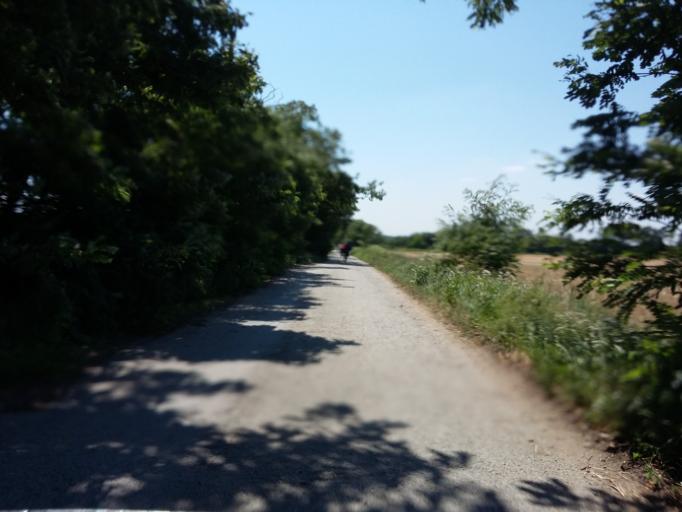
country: AT
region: Lower Austria
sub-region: Politischer Bezirk Ganserndorf
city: Marchegg
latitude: 48.2879
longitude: 16.9677
